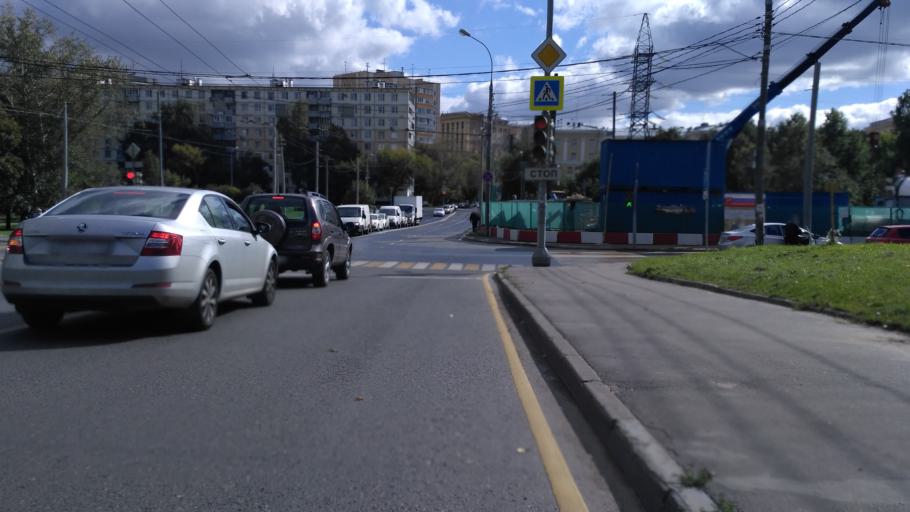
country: RU
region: Moscow
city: Ostankinskiy
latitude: 55.8162
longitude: 37.6310
